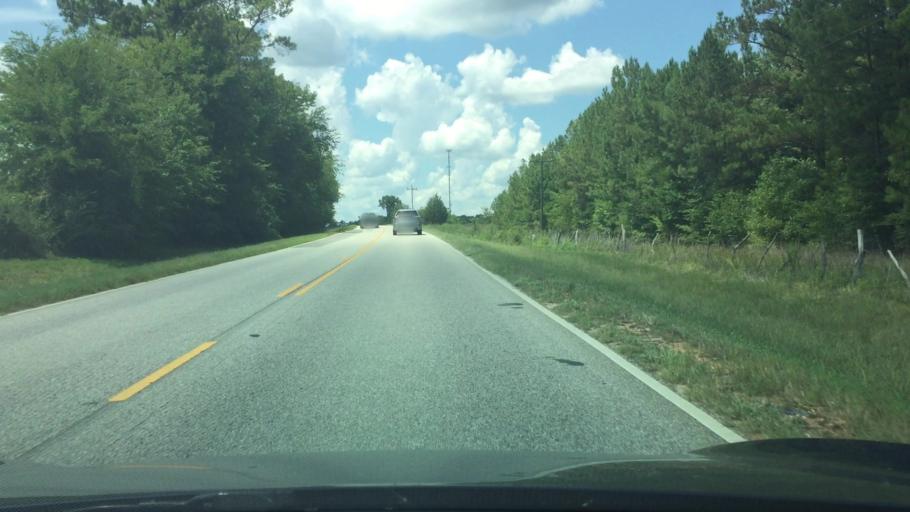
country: US
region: Alabama
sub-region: Montgomery County
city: Pike Road
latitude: 32.1999
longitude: -86.1056
